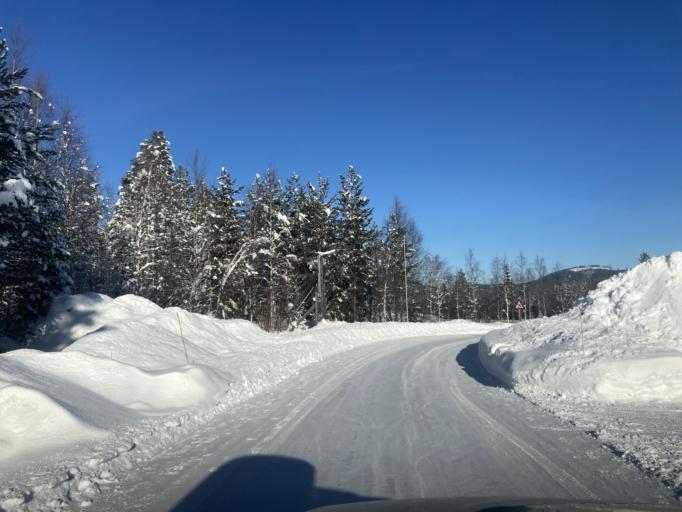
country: NO
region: Hedmark
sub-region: Trysil
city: Innbygda
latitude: 61.2998
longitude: 12.2441
